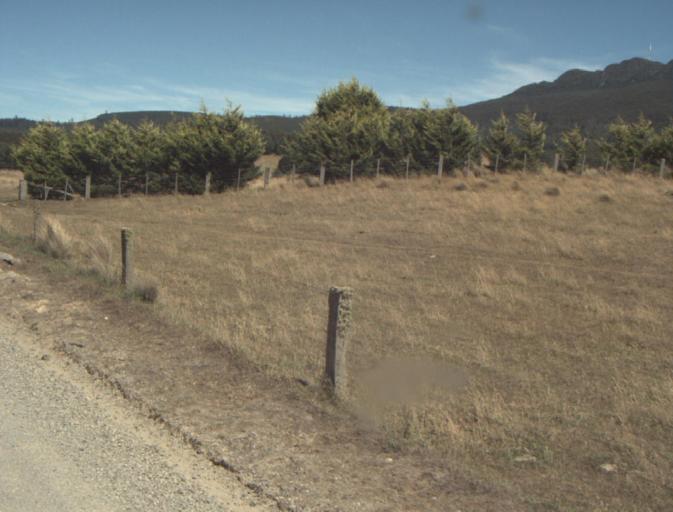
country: AU
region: Tasmania
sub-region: Dorset
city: Scottsdale
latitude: -41.3488
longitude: 147.4487
